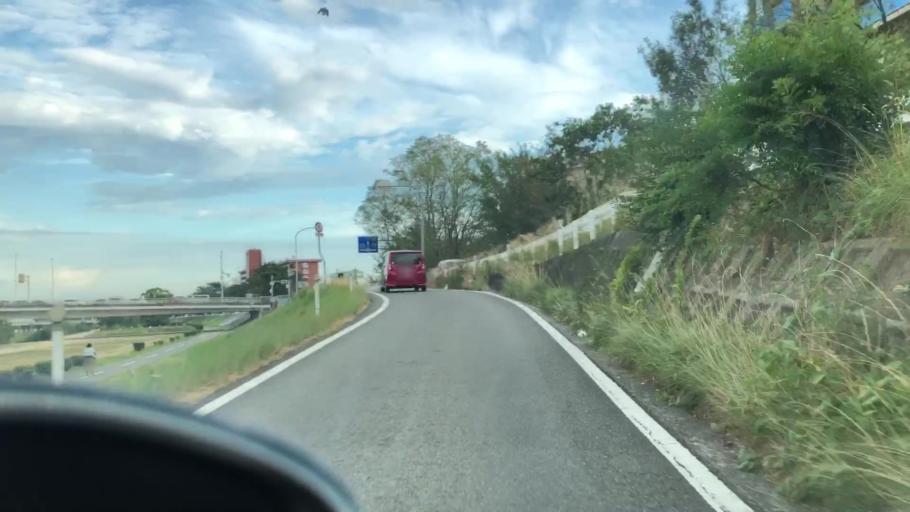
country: JP
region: Hyogo
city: Itami
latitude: 34.7441
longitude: 135.3758
